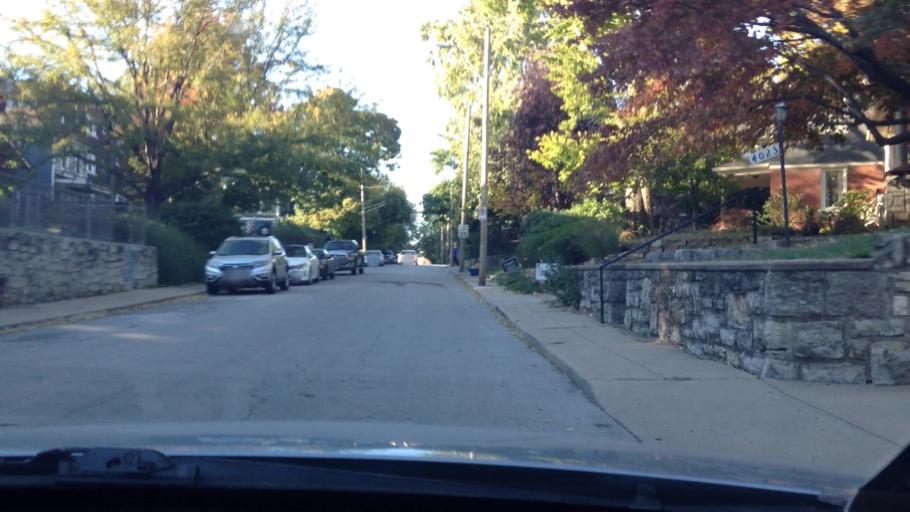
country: US
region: Kansas
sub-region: Johnson County
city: Westwood
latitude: 39.0542
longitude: -94.5969
